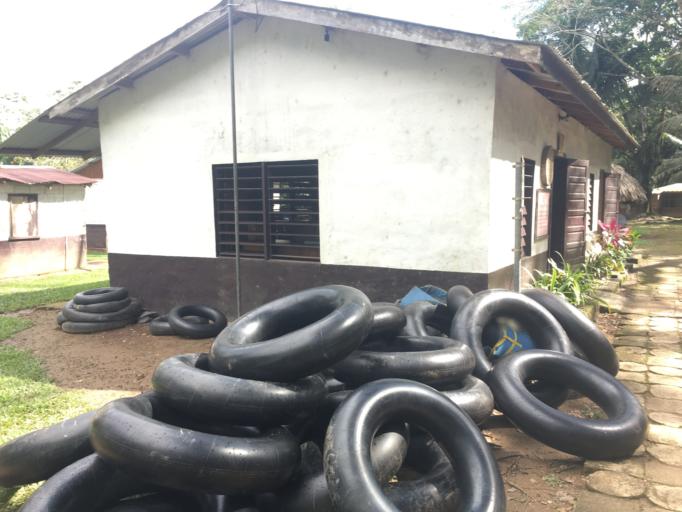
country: BZ
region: Stann Creek
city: Placencia
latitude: 16.7808
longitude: -88.4589
